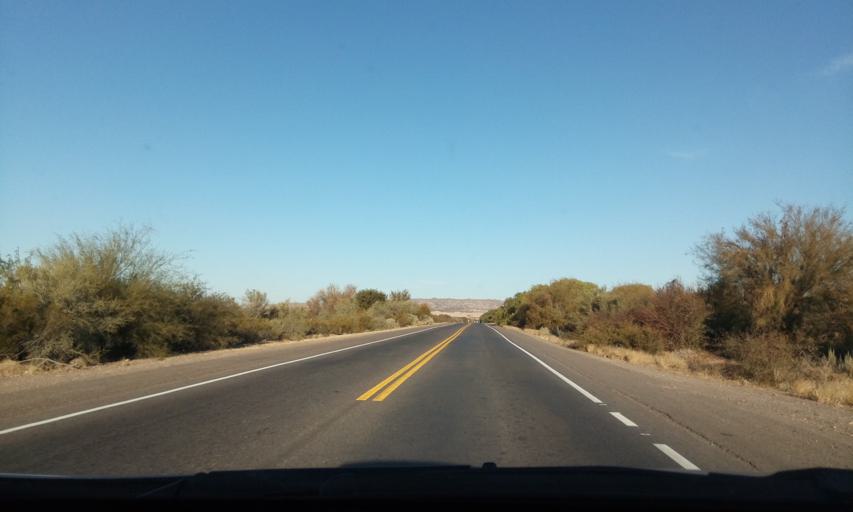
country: AR
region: San Juan
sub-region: Departamento de Rivadavia
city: Rivadavia
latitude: -31.4313
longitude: -68.6651
